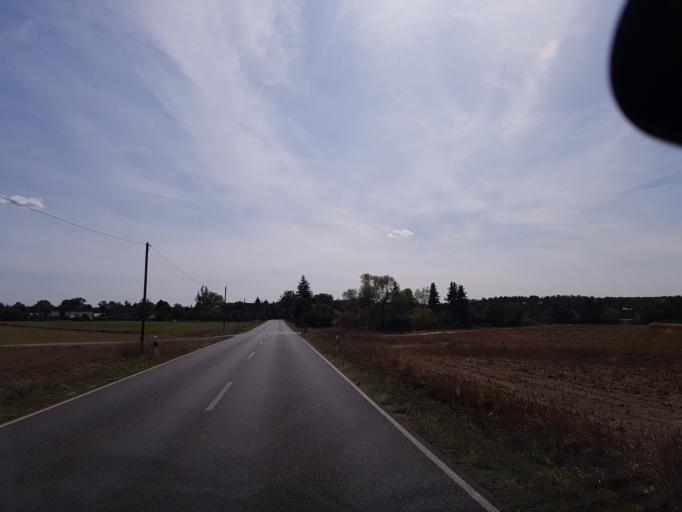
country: DE
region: Brandenburg
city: Luckau
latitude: 51.7779
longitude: 13.6887
